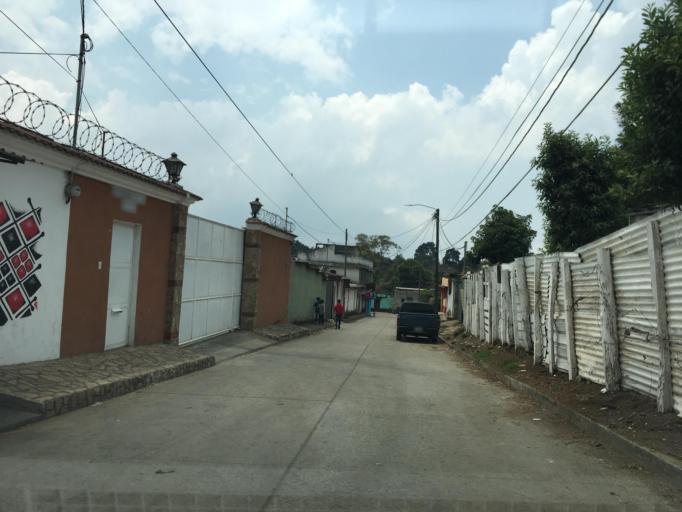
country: GT
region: Guatemala
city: Villa Canales
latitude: 14.4050
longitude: -90.5473
